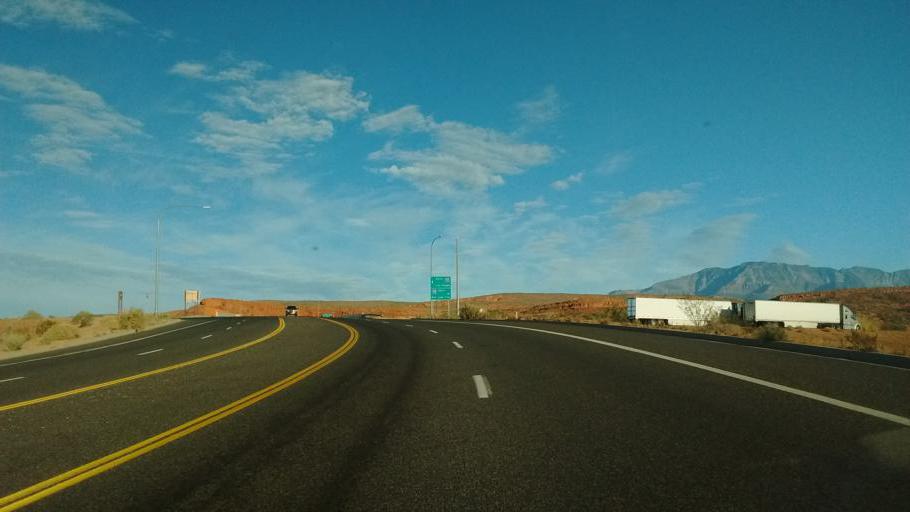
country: US
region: Utah
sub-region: Washington County
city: Washington
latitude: 37.1458
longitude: -113.4863
